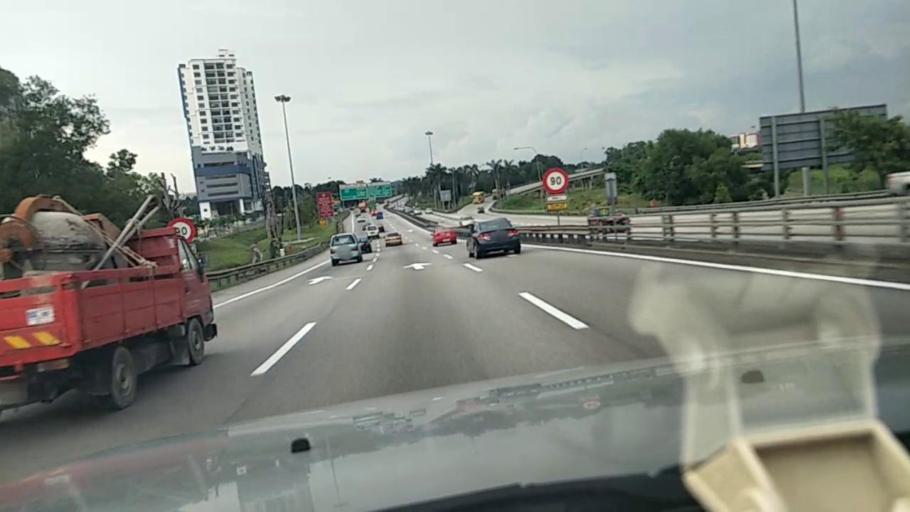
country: MY
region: Selangor
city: Shah Alam
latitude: 3.0872
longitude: 101.5507
